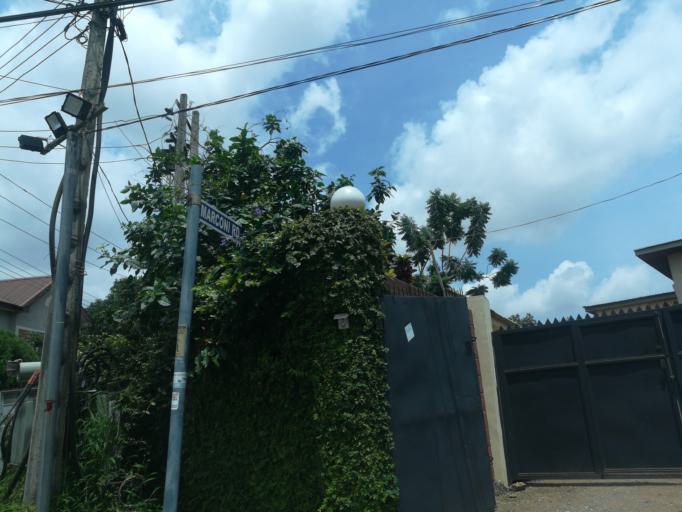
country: NG
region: Lagos
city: Somolu
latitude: 6.5418
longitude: 3.3636
